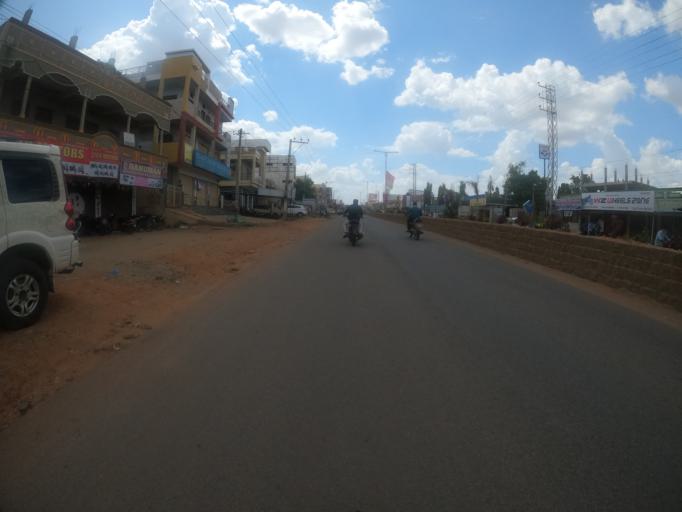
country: IN
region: Telangana
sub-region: Rangareddi
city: Sriramnagar
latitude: 17.3088
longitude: 78.1428
